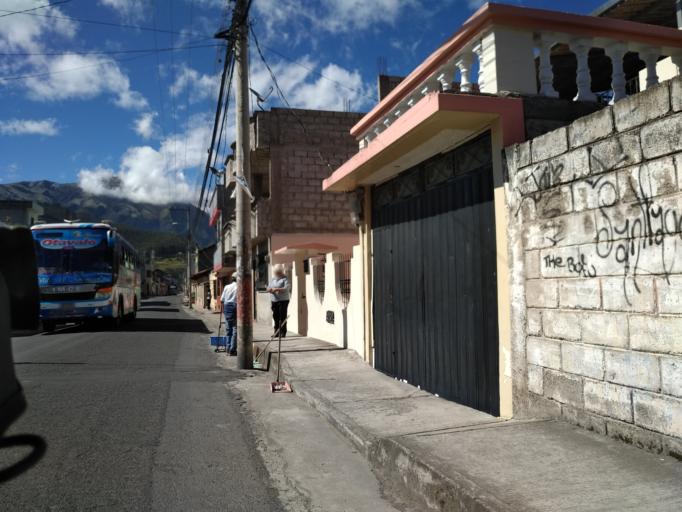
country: EC
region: Imbabura
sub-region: Canton Otavalo
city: Otavalo
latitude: 0.1991
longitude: -78.1929
